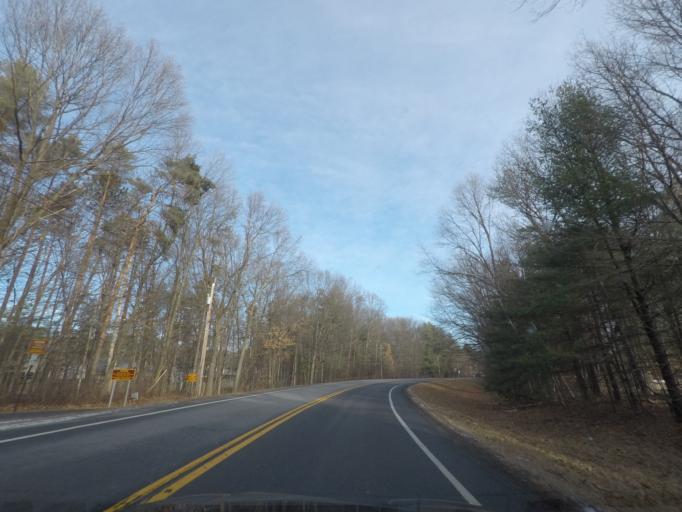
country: US
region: New York
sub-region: Saratoga County
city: Country Knolls
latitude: 42.9749
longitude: -73.7744
